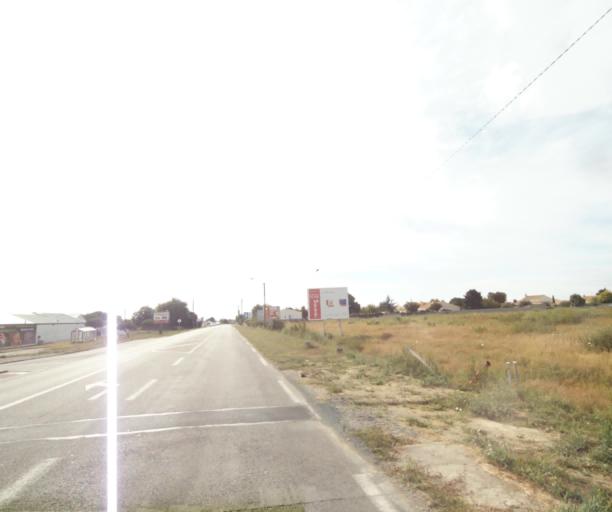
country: FR
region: Pays de la Loire
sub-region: Departement de la Vendee
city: Chateau-d'Olonne
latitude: 46.4857
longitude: -1.7346
